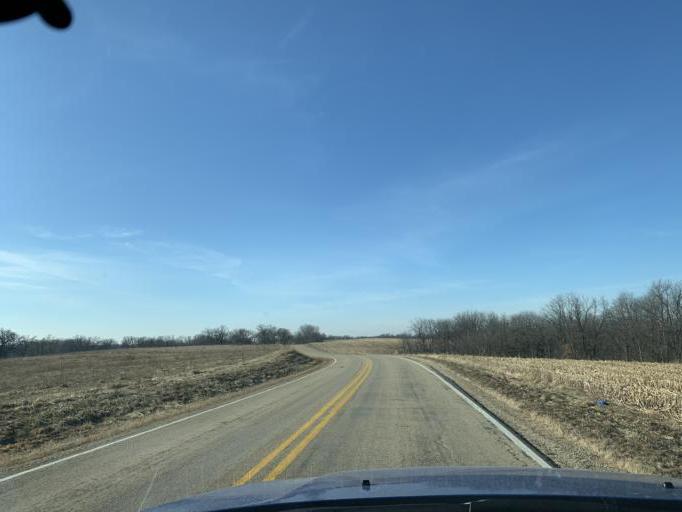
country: US
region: Wisconsin
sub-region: Iowa County
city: Barneveld
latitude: 42.8145
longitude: -89.9072
